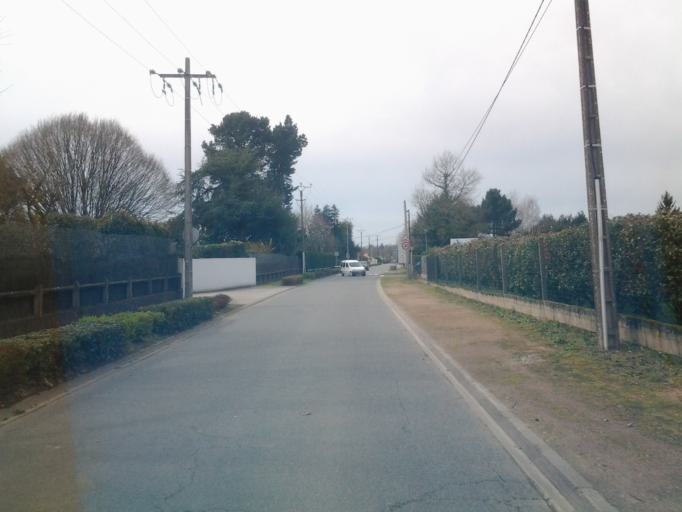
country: FR
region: Pays de la Loire
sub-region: Departement de la Vendee
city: Venansault
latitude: 46.6860
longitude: -1.5192
